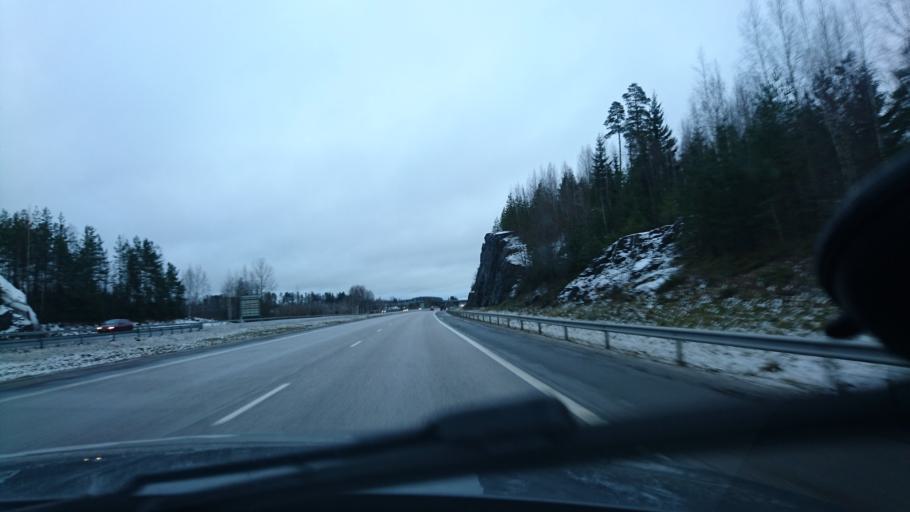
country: FI
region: Uusimaa
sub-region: Helsinki
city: Maentsaelae
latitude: 60.6384
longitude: 25.2981
